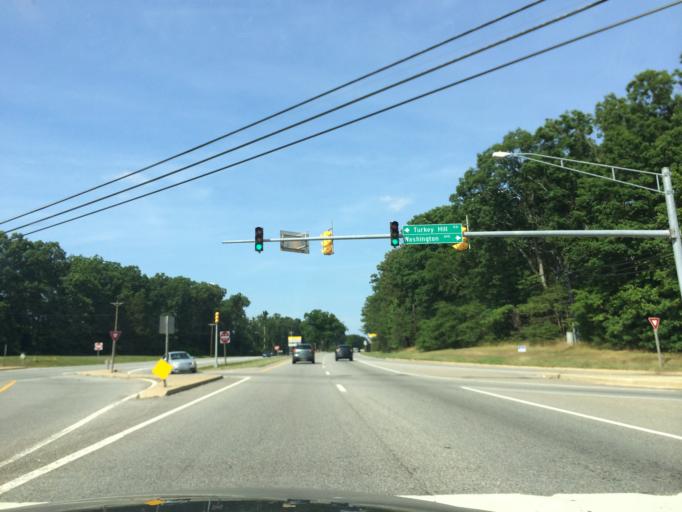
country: US
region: Maryland
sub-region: Charles County
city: La Plata
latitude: 38.5686
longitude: -76.9811
